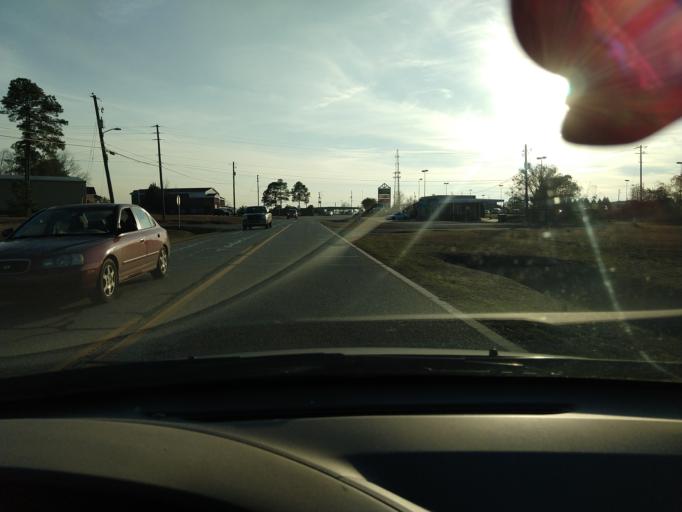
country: US
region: Georgia
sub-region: Sumter County
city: Americus
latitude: 32.0756
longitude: -84.2153
